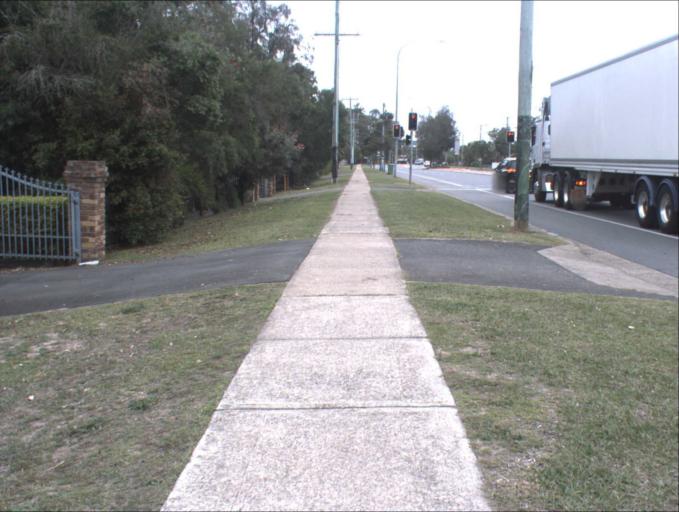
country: AU
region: Queensland
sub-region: Logan
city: Park Ridge South
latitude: -27.6834
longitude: 153.0175
